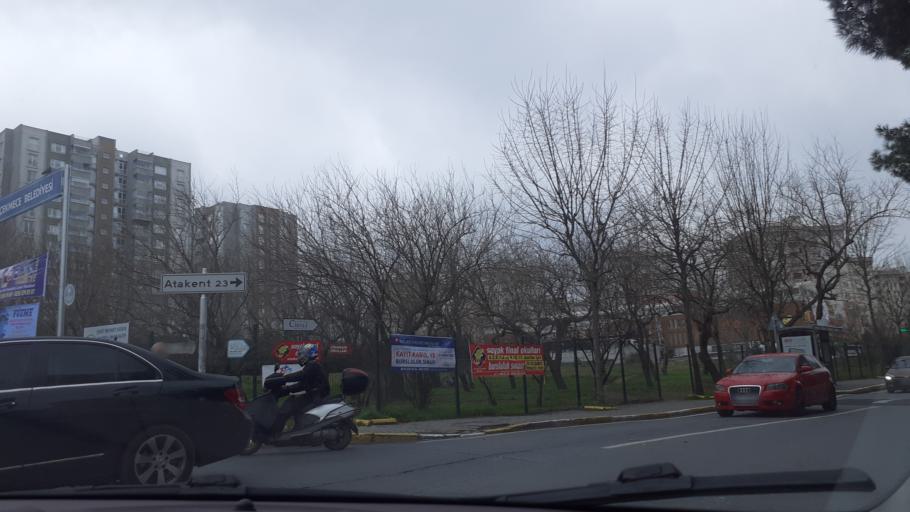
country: TR
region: Istanbul
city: Mahmutbey
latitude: 41.0491
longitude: 28.7852
